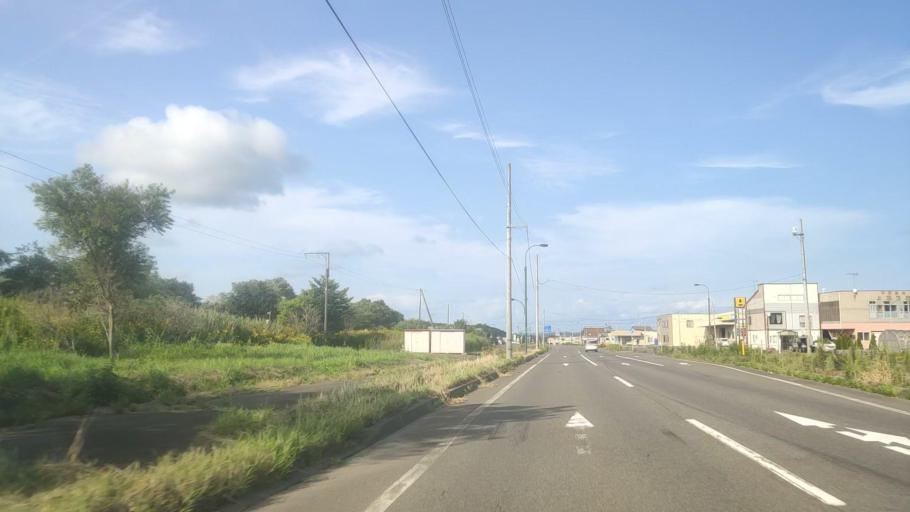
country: JP
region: Hokkaido
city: Chitose
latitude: 42.7630
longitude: 141.8117
